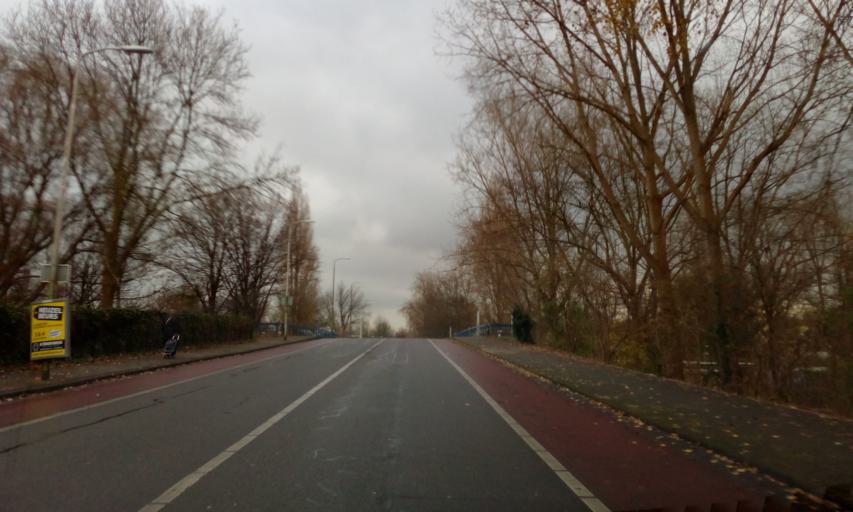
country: NL
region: South Holland
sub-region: Gemeente Zoetermeer
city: Zoetermeer
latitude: 52.0515
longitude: 4.4864
